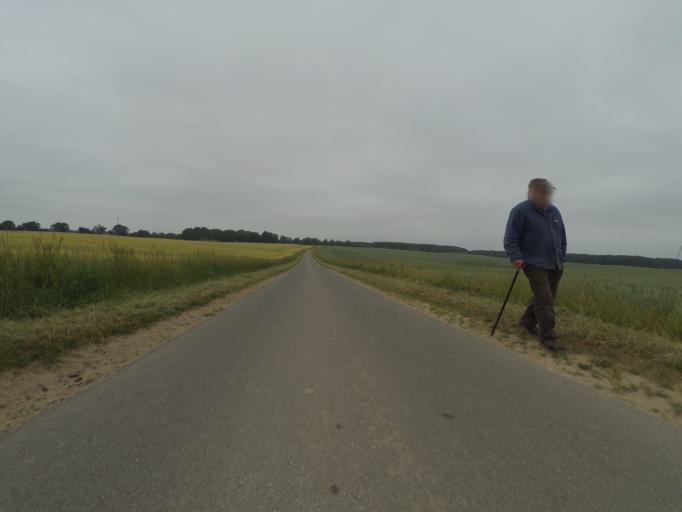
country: DE
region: Mecklenburg-Vorpommern
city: Goldberg
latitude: 53.5499
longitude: 12.0348
